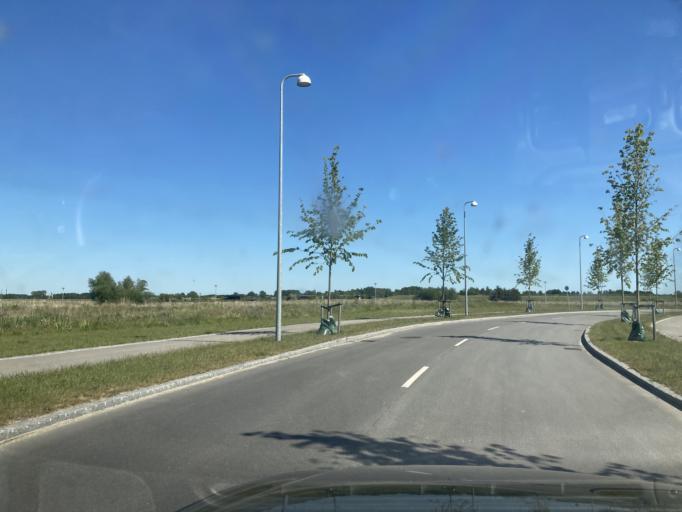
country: DK
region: Zealand
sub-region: Greve Kommune
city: Greve
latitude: 55.5980
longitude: 12.2697
